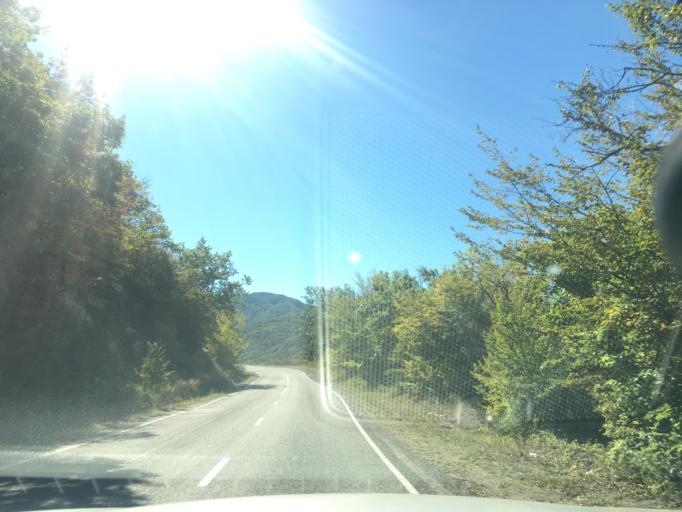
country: GE
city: Didi Lilo
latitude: 41.8669
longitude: 44.9167
